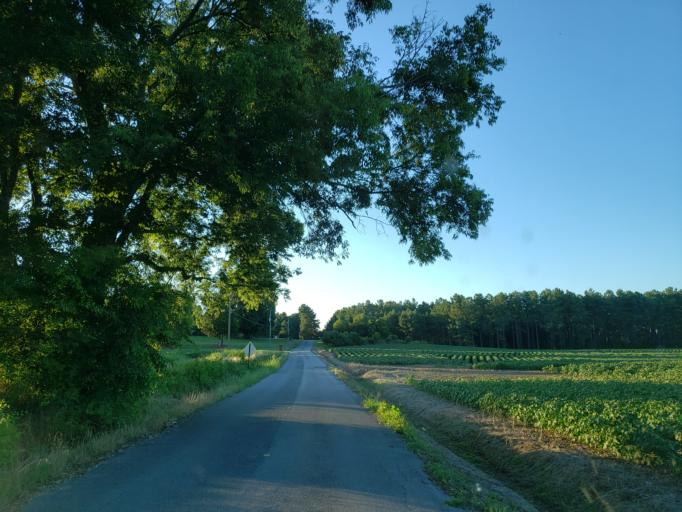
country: US
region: Georgia
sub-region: Bartow County
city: Euharlee
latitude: 34.0733
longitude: -84.9636
